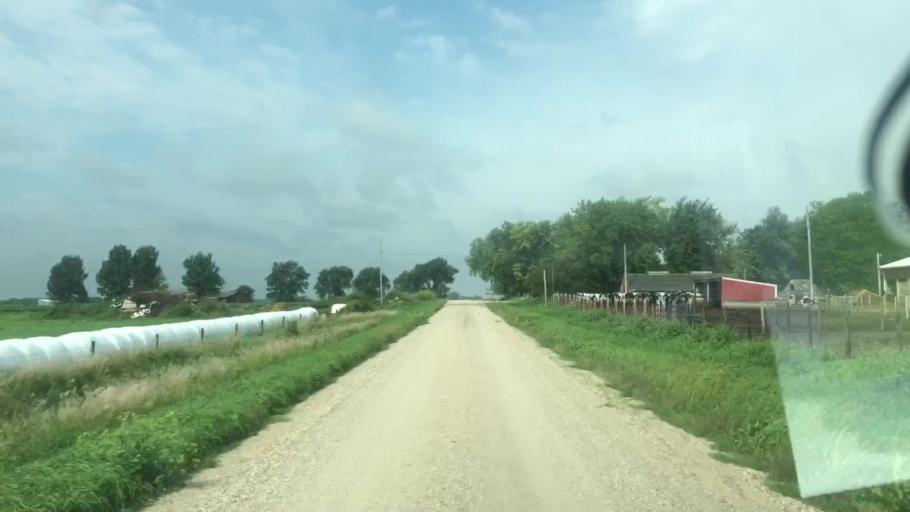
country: US
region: Iowa
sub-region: O'Brien County
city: Sheldon
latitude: 43.2724
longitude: -95.9174
